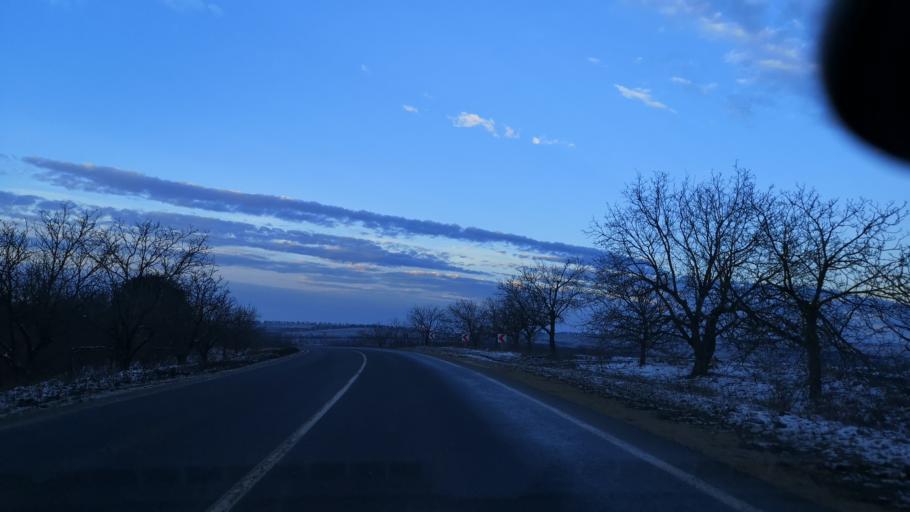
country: MD
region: Orhei
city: Orhei
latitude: 47.5597
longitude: 28.7994
